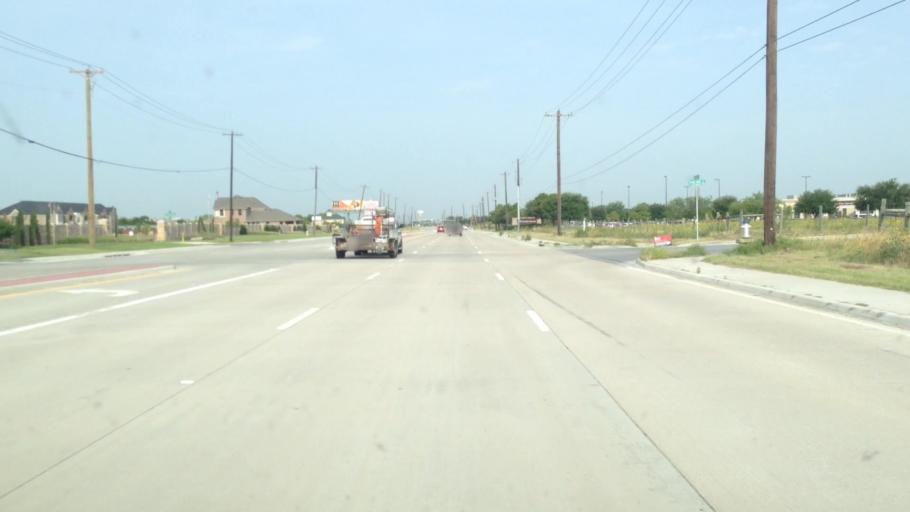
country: US
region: Texas
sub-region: Denton County
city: The Colony
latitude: 33.0449
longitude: -96.8661
